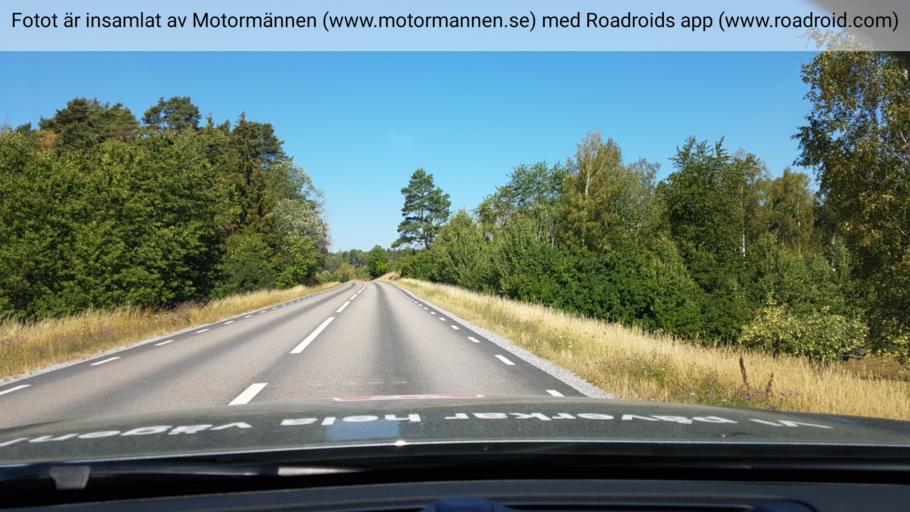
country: SE
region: Stockholm
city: Stenhamra
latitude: 59.3766
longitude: 17.5973
